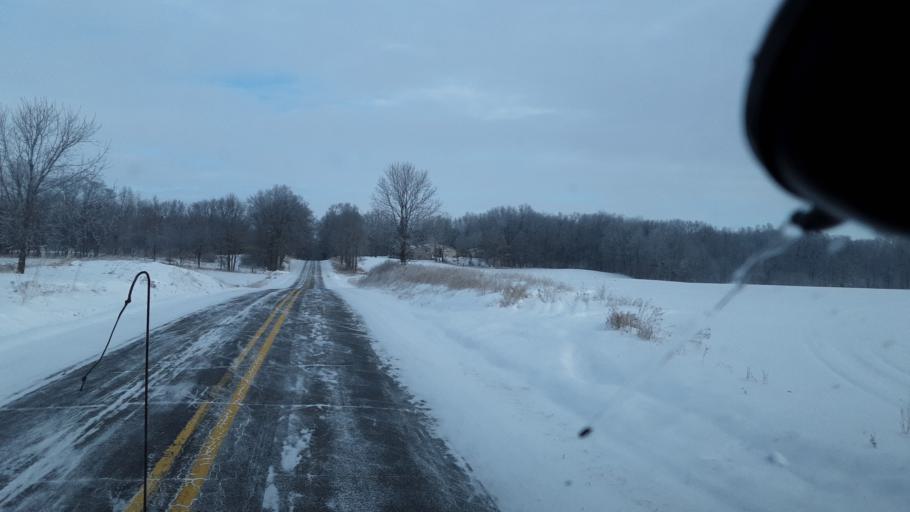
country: US
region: Michigan
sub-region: Ingham County
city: Leslie
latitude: 42.3595
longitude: -84.4826
